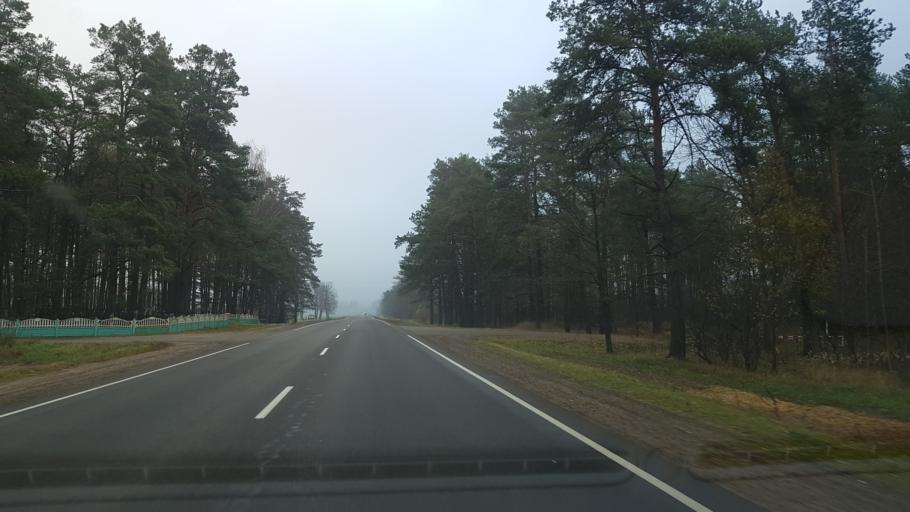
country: BY
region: Mogilev
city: Babruysk
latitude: 53.1666
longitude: 29.3309
